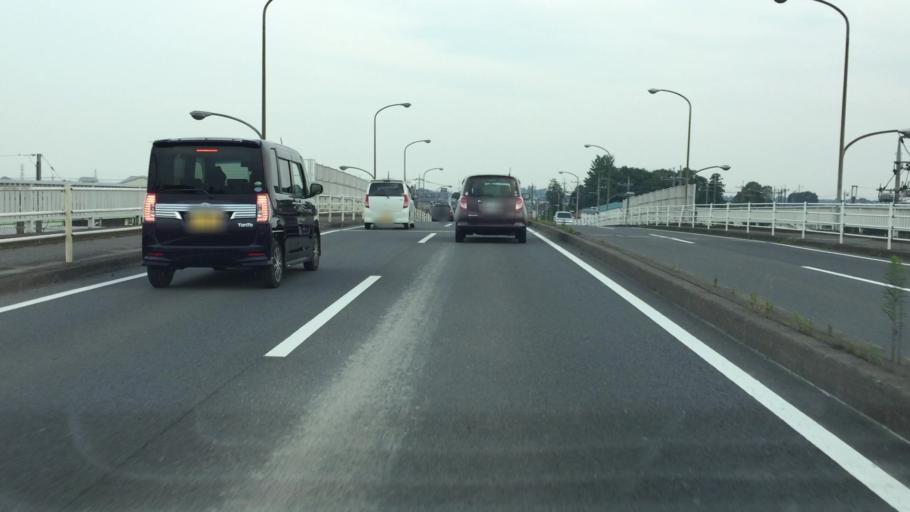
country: JP
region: Tochigi
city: Tochigi
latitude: 36.3643
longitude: 139.7165
